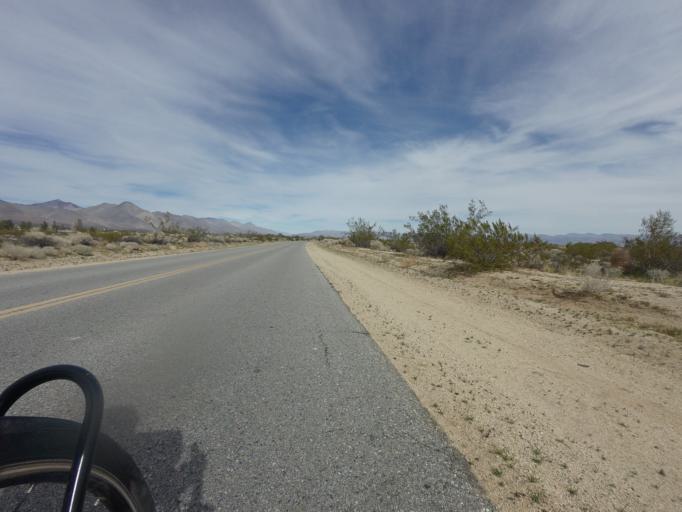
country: US
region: California
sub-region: Kern County
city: Inyokern
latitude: 35.7154
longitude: -117.8330
